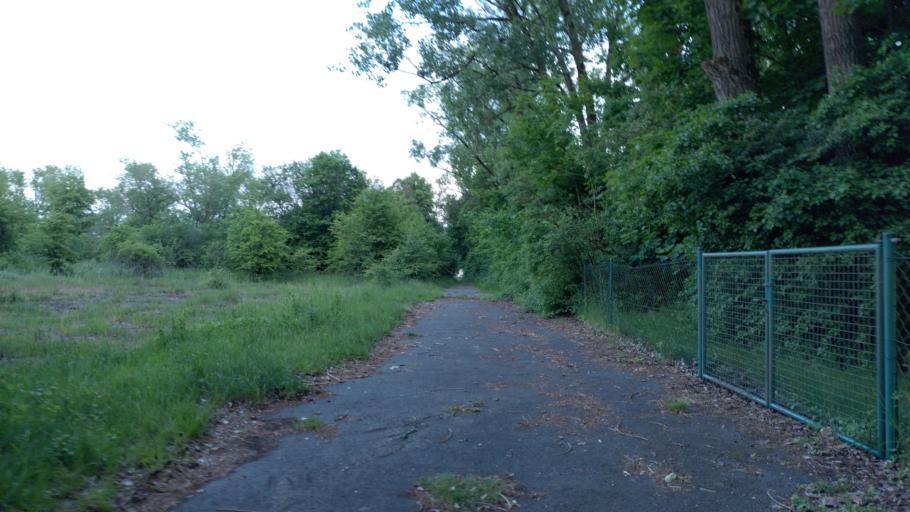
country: DE
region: Bavaria
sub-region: Upper Franconia
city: Bindlach
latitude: 49.9948
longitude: 11.6178
